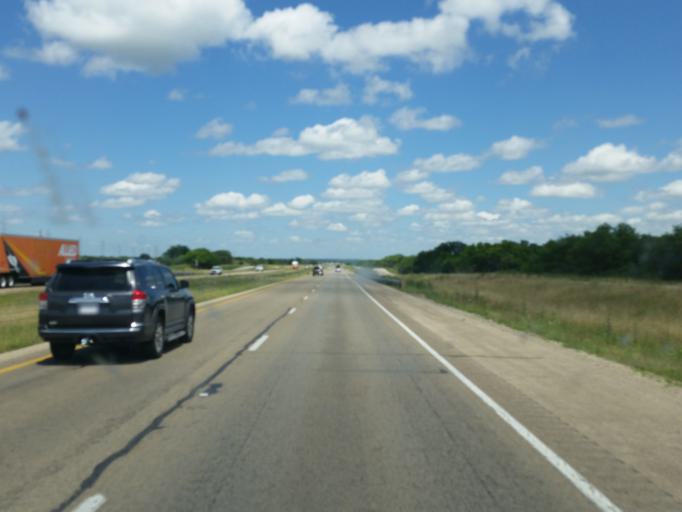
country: US
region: Texas
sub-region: Callahan County
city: Baird
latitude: 32.3903
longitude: -99.3355
